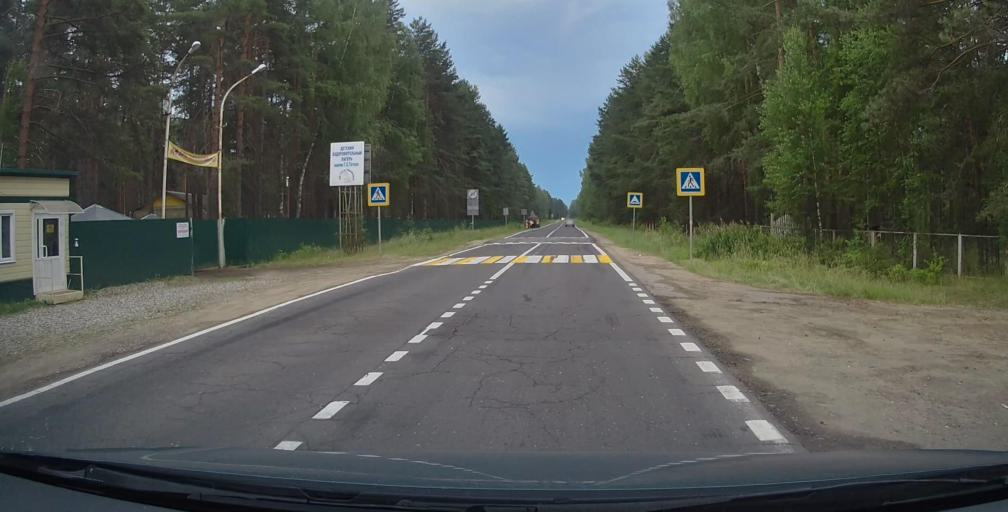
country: RU
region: Jaroslavl
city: Myshkin
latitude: 57.7886
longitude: 38.4938
